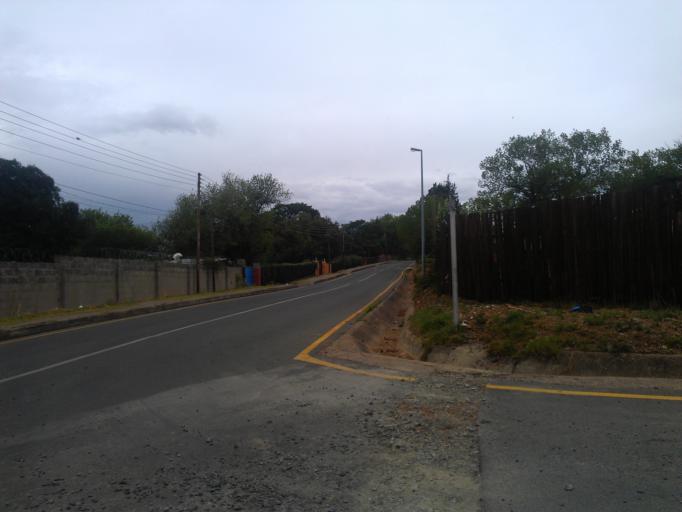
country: LS
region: Maseru
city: Maseru
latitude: -29.3022
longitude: 27.4690
